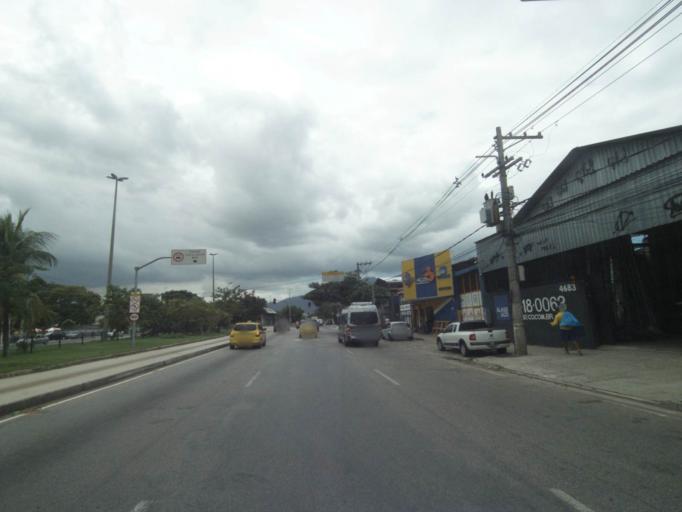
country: BR
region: Rio de Janeiro
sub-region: Nilopolis
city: Nilopolis
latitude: -22.9591
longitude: -43.3848
